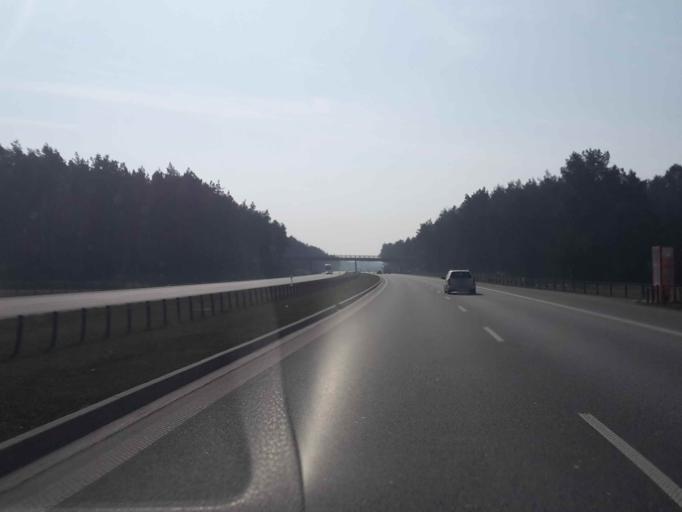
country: PL
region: Kujawsko-Pomorskie
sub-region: Powiat torunski
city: Lubicz Dolny
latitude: 52.9981
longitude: 18.7326
